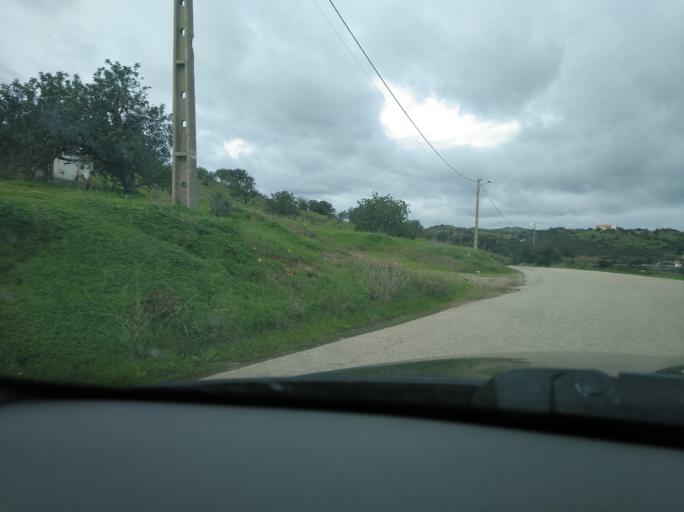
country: PT
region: Faro
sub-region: Castro Marim
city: Castro Marim
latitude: 37.2229
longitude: -7.4901
